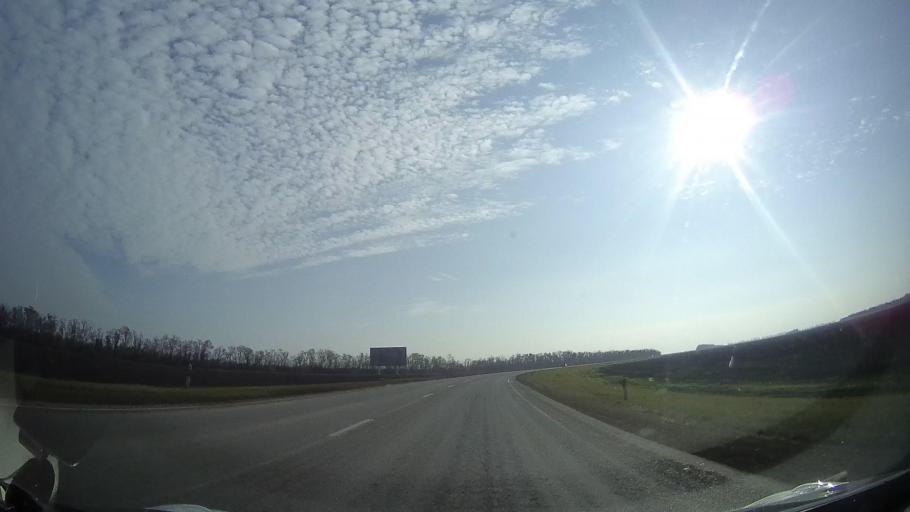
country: RU
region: Rostov
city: Tselina
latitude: 46.5309
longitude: 40.9878
